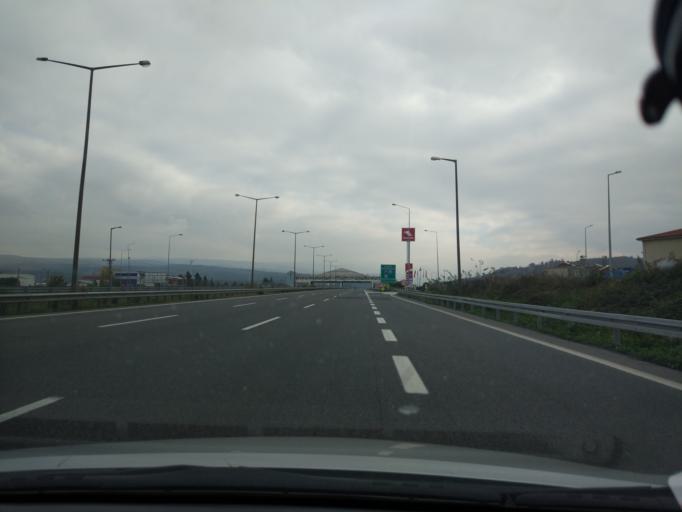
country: TR
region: Duzce
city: Duzce
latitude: 40.7905
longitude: 31.2355
